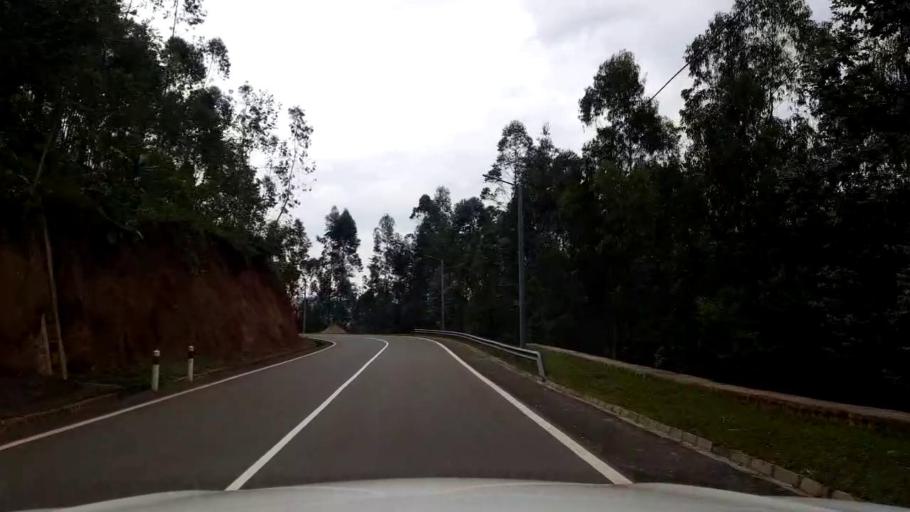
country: RW
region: Western Province
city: Kibuye
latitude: -1.9248
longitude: 29.3683
